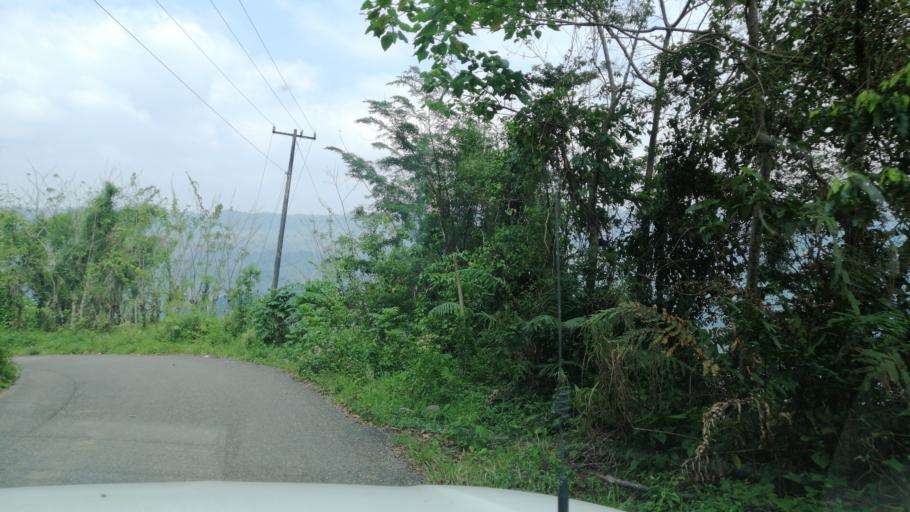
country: MX
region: Chiapas
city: Ostuacan
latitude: 17.3911
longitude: -93.3355
